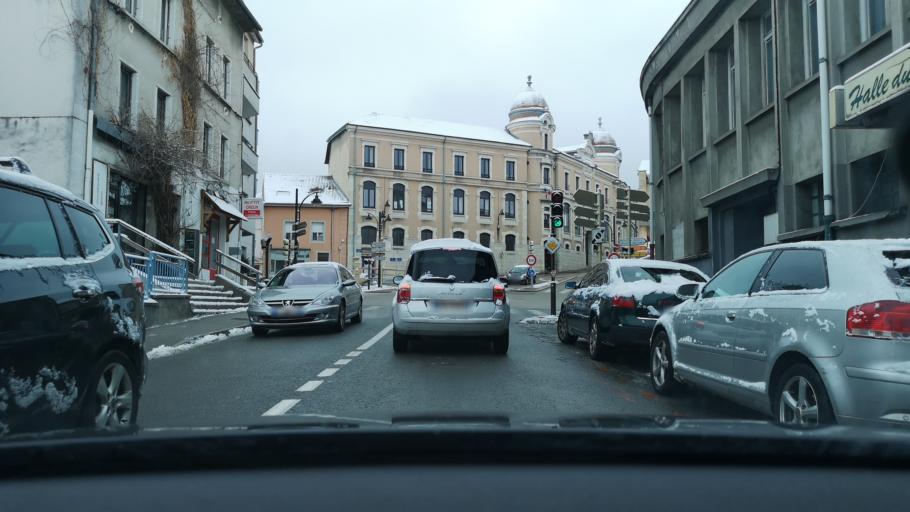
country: FR
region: Rhone-Alpes
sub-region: Departement de l'Ain
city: Oyonnax
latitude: 46.2591
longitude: 5.6582
